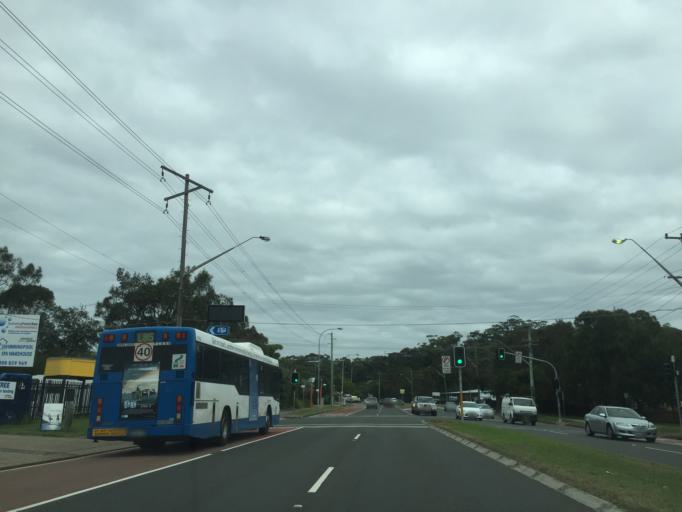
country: AU
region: New South Wales
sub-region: Pittwater
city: North Narrabeen
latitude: -33.7015
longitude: 151.2989
